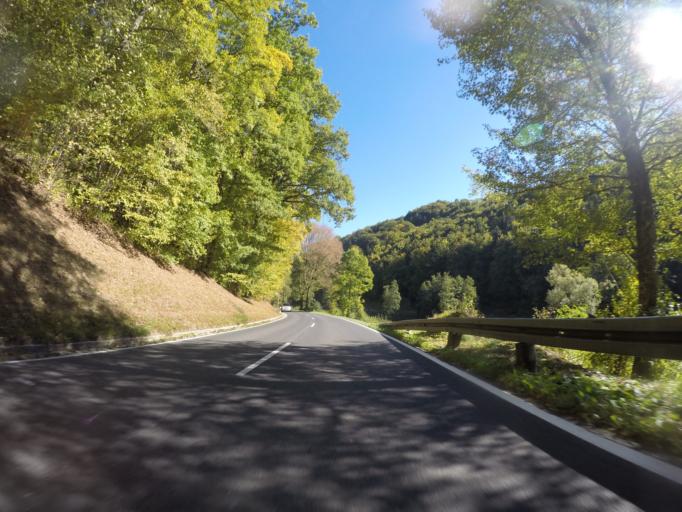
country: DE
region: Bavaria
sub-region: Upper Franconia
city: Gossweinstein
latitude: 49.7709
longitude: 11.3163
